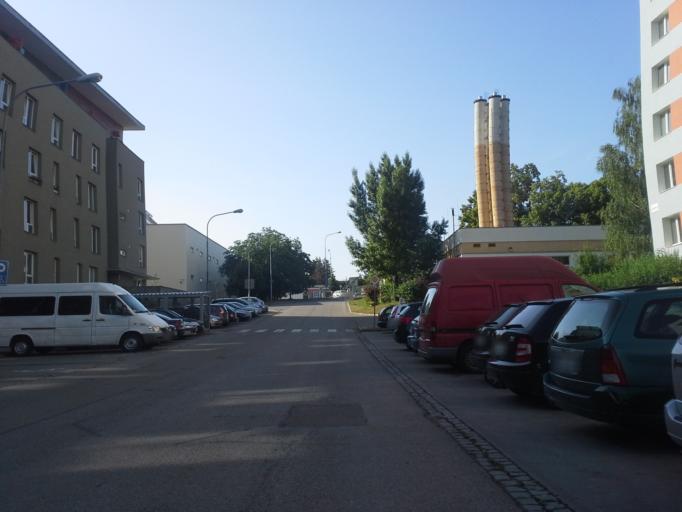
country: CZ
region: South Moravian
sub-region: Mesto Brno
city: Mokra Hora
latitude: 49.2369
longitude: 16.5841
